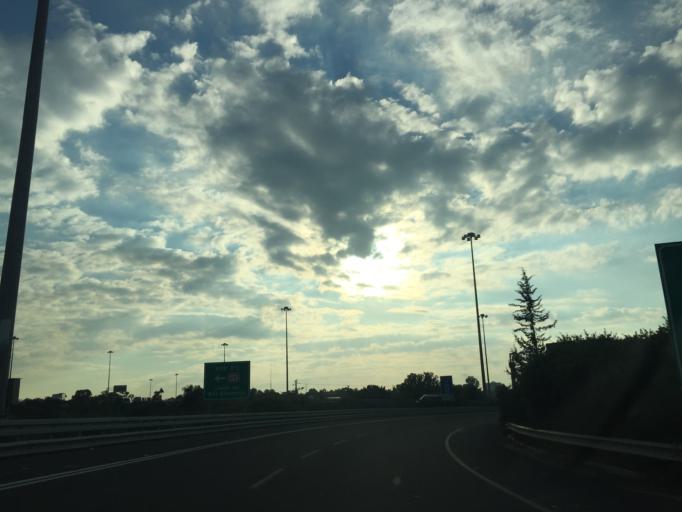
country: IL
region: Central District
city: Ramla
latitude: 31.9258
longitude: 34.8857
